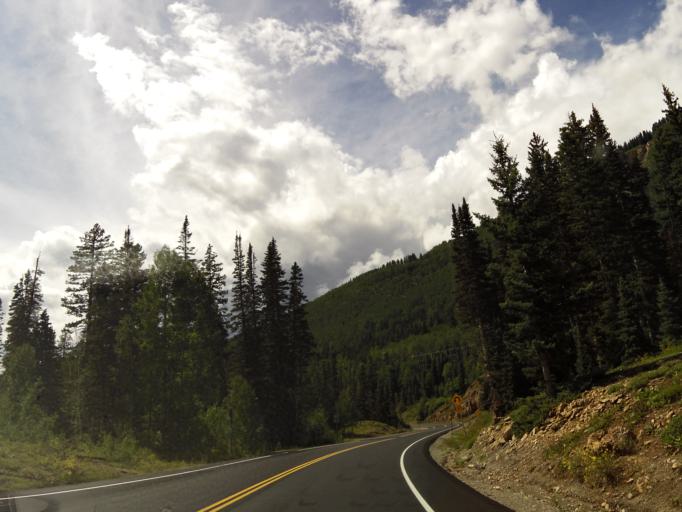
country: US
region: Colorado
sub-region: San Juan County
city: Silverton
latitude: 37.6789
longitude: -107.7931
